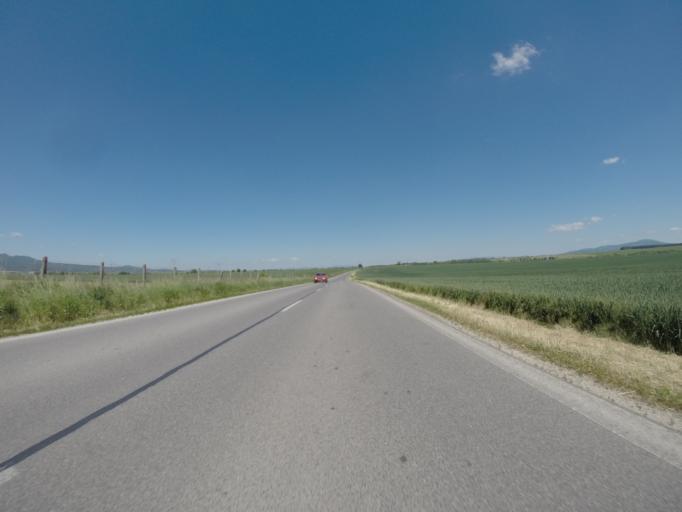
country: SK
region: Trnavsky
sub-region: Okres Trnava
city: Piestany
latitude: 48.5129
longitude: 17.9947
